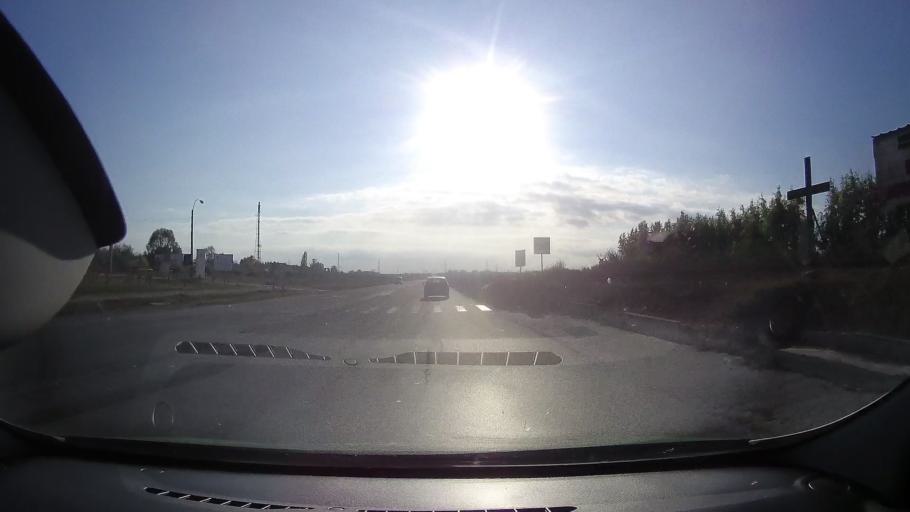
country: RO
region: Constanta
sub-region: Comuna Navodari
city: Navodari
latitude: 44.3357
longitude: 28.6340
